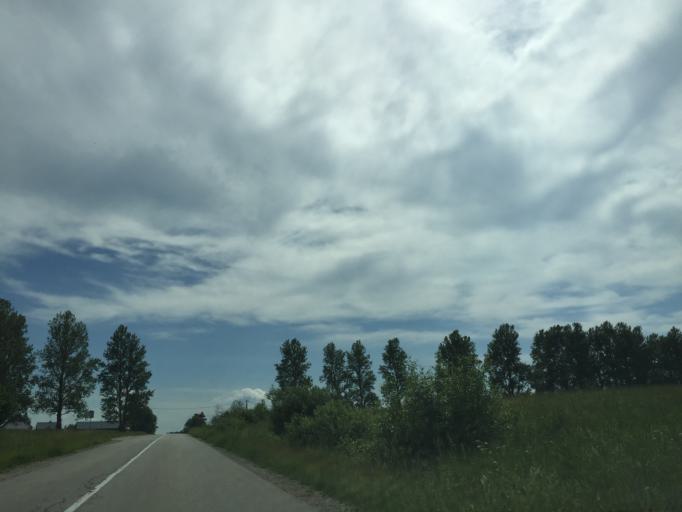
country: LV
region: Tukuma Rajons
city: Tukums
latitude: 57.0322
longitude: 23.2511
